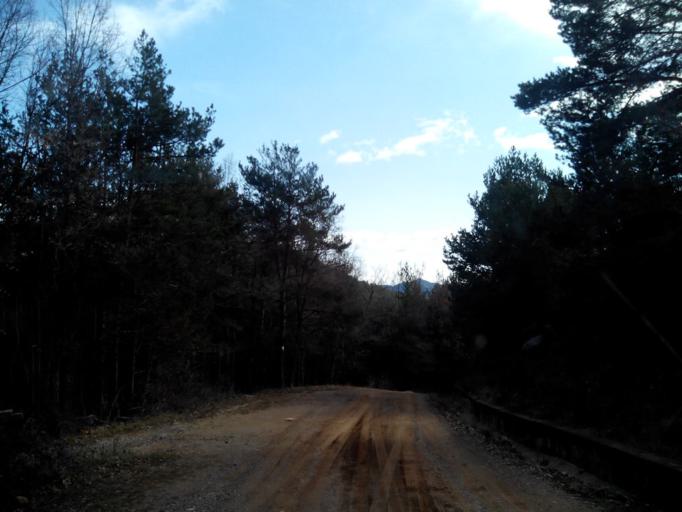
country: ES
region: Catalonia
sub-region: Provincia de Barcelona
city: Vilada
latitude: 42.1592
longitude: 1.9284
